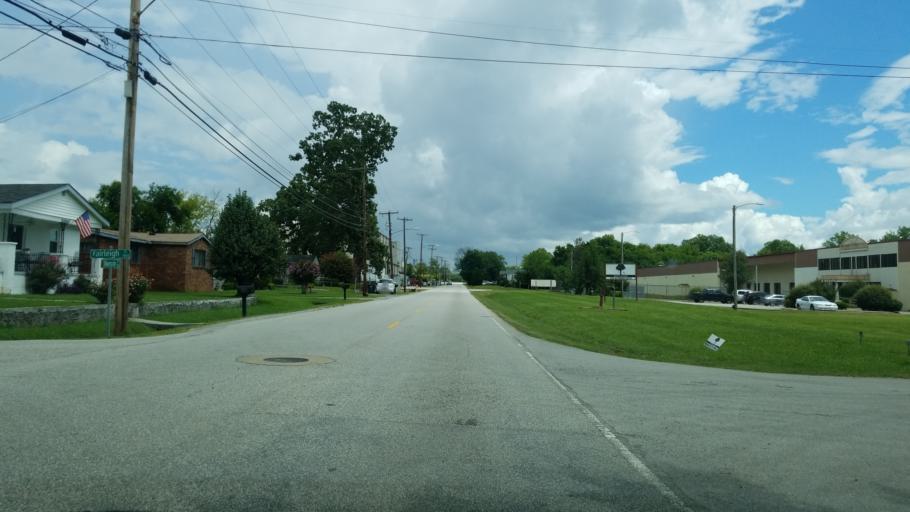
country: US
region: Tennessee
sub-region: Hamilton County
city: East Chattanooga
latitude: 35.0712
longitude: -85.2604
